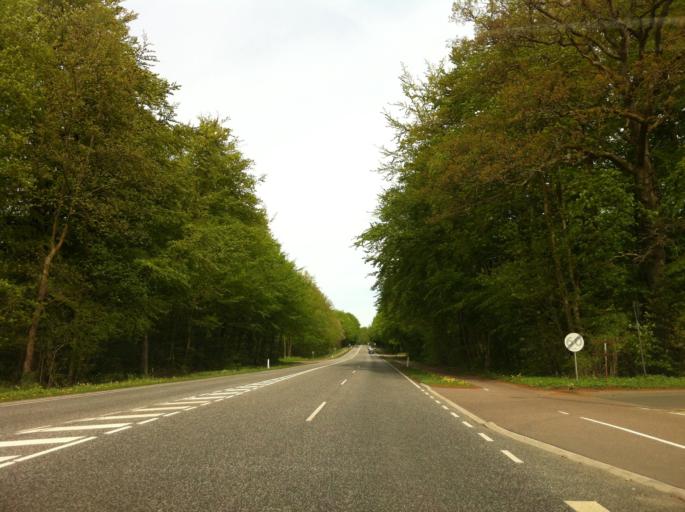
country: DK
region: Capital Region
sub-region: Allerod Kommune
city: Blovstrod
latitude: 55.8758
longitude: 12.3750
